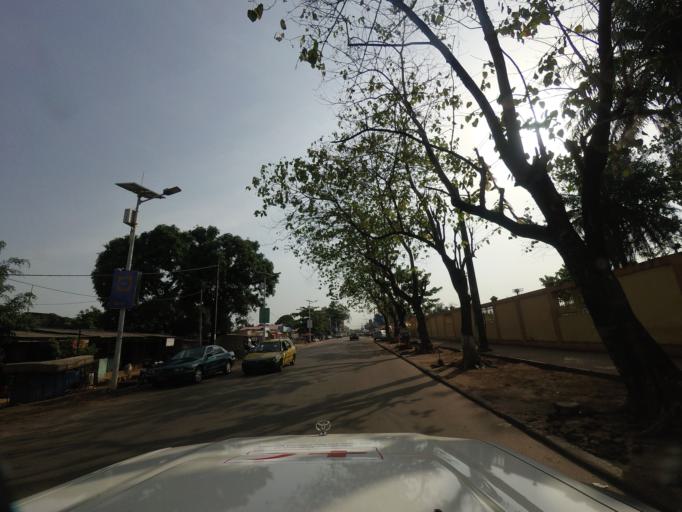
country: GN
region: Conakry
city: Conakry
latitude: 9.5468
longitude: -13.6768
